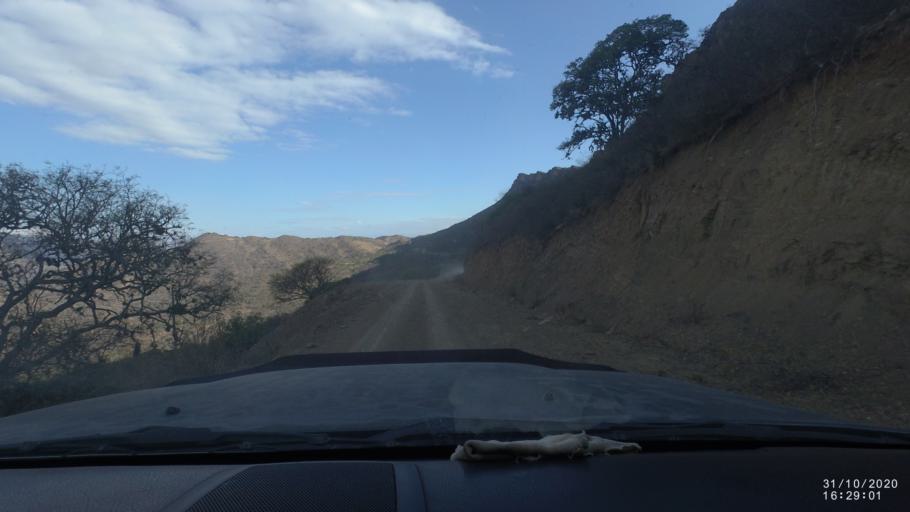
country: BO
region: Chuquisaca
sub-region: Provincia Zudanez
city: Mojocoya
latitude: -18.4166
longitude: -64.5863
